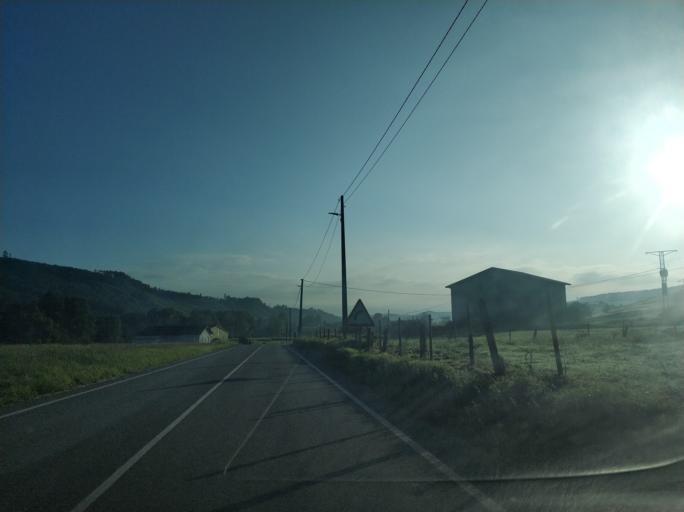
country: ES
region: Cantabria
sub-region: Provincia de Cantabria
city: Polanco
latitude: 43.3845
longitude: -3.9679
